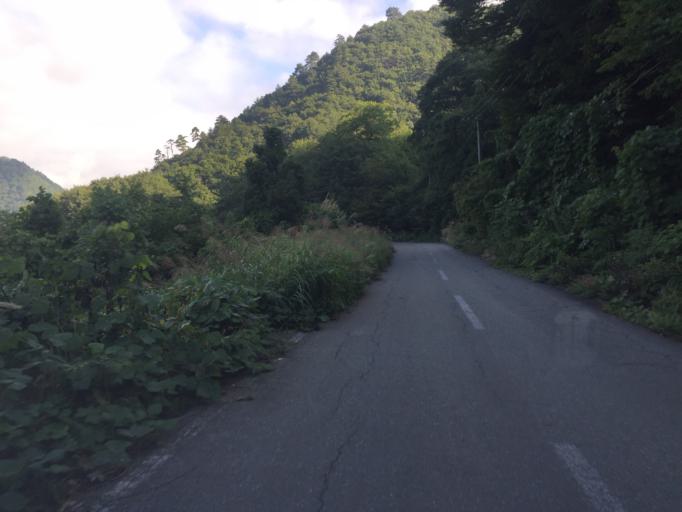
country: JP
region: Fukushima
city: Inawashiro
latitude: 37.4473
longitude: 139.9677
